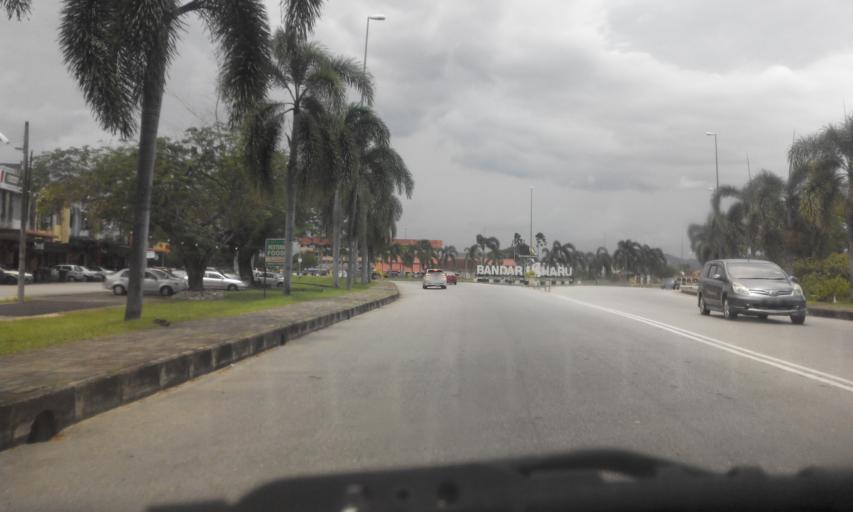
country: MY
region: Perak
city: Parit Buntar
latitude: 5.1305
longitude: 100.4964
